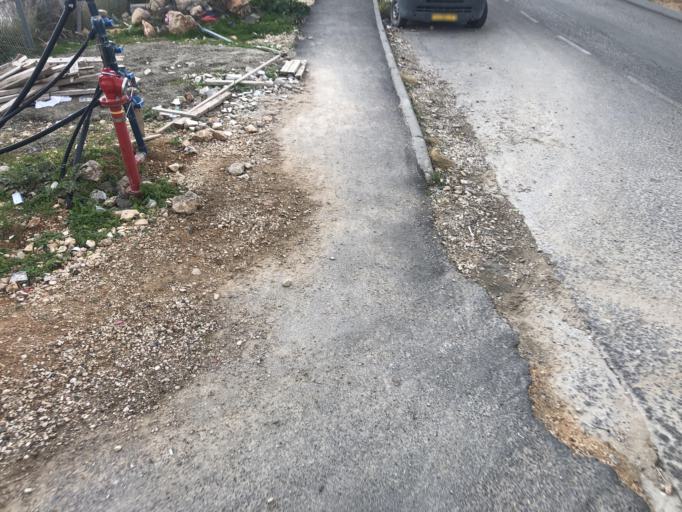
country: IL
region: Jerusalem
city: Modiin Ilit
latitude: 31.9368
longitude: 35.0470
